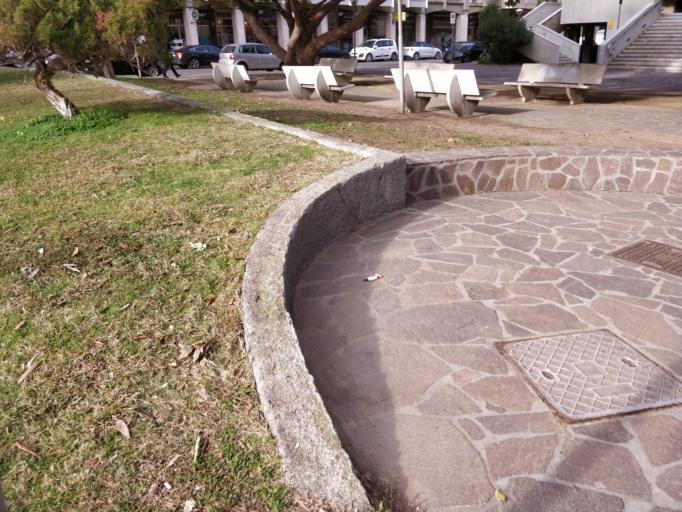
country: IT
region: Liguria
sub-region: Provincia di Savona
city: Andora
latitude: 43.9519
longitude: 8.1466
